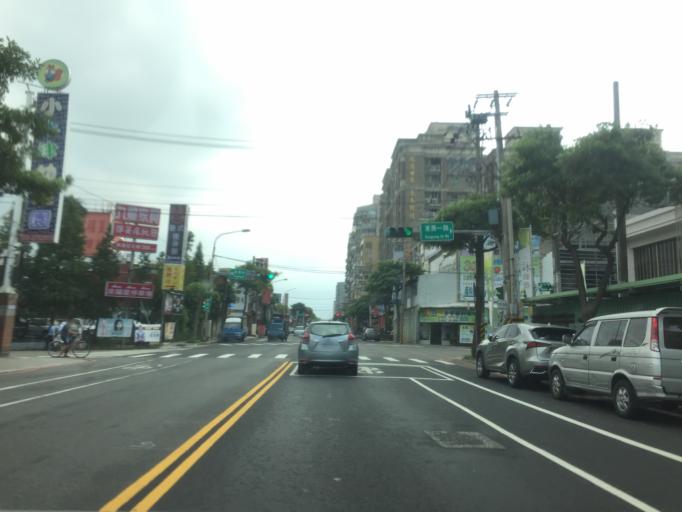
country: TW
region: Taiwan
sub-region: Taoyuan
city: Taoyuan
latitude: 24.9649
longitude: 121.3068
